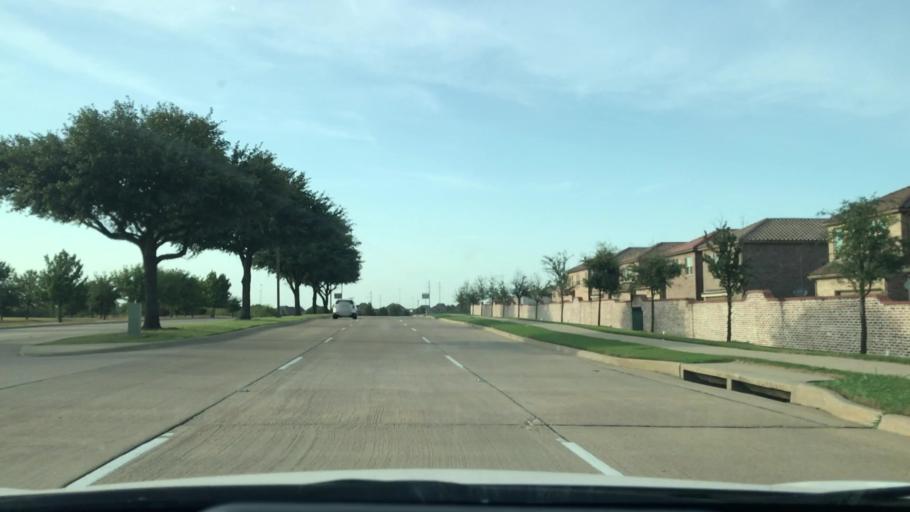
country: US
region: Texas
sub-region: Dallas County
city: Farmers Branch
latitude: 32.8995
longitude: -96.9452
